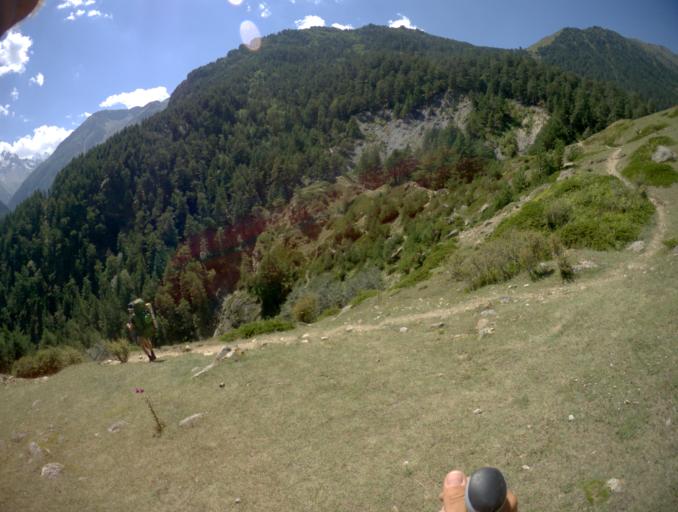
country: RU
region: Kabardino-Balkariya
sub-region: El'brusskiy Rayon
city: El'brus
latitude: 43.2644
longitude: 42.6359
